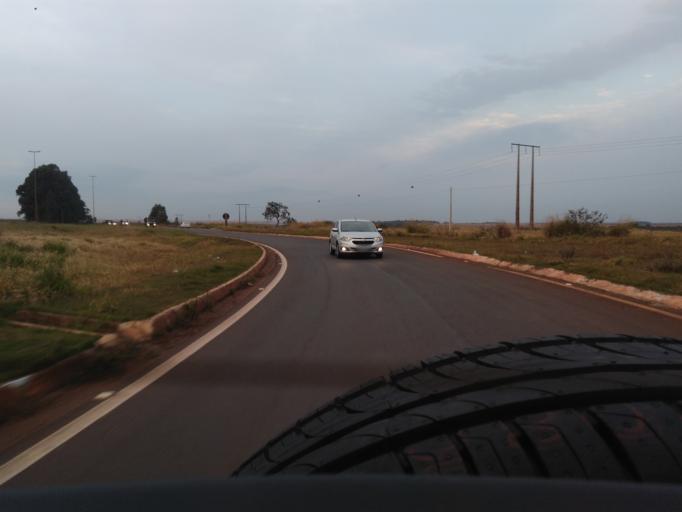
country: BR
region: Mato Grosso do Sul
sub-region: Dourados
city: Dourados
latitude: -22.3015
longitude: -55.1014
